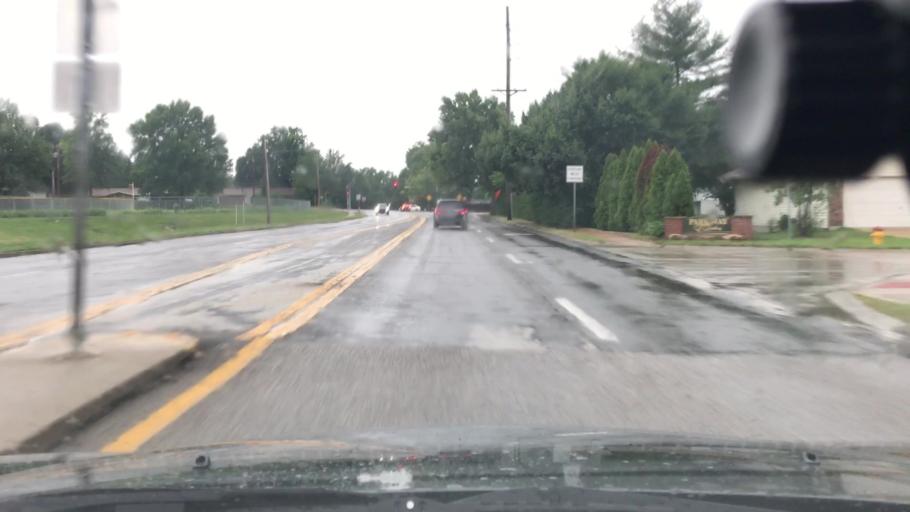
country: US
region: Missouri
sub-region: Saint Louis County
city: Maryland Heights
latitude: 38.6944
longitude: -90.4648
